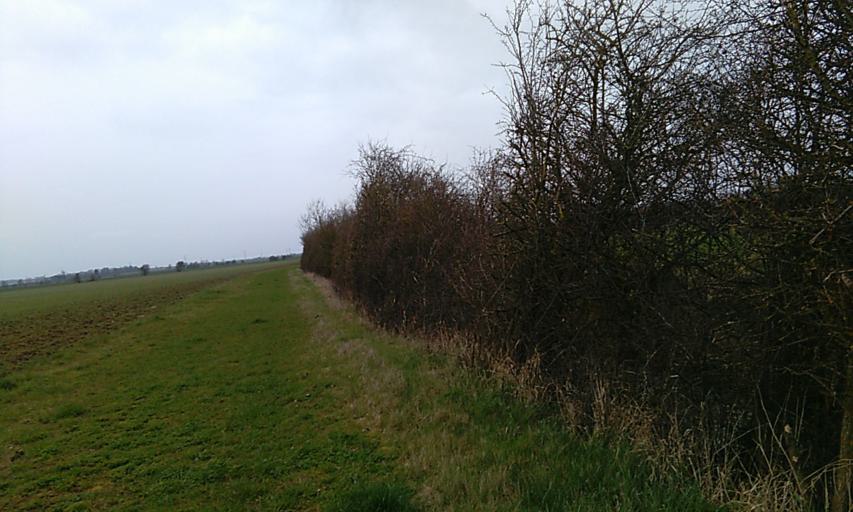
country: GB
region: England
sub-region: Nottinghamshire
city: Bingham
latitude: 52.9149
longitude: -0.9352
